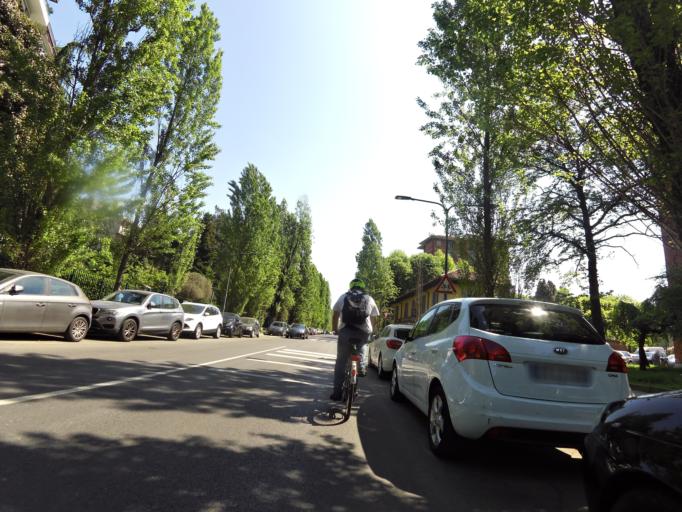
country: IT
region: Lombardy
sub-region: Citta metropolitana di Milano
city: Novegro-Tregarezzo-San Felice
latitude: 45.4914
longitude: 9.2439
